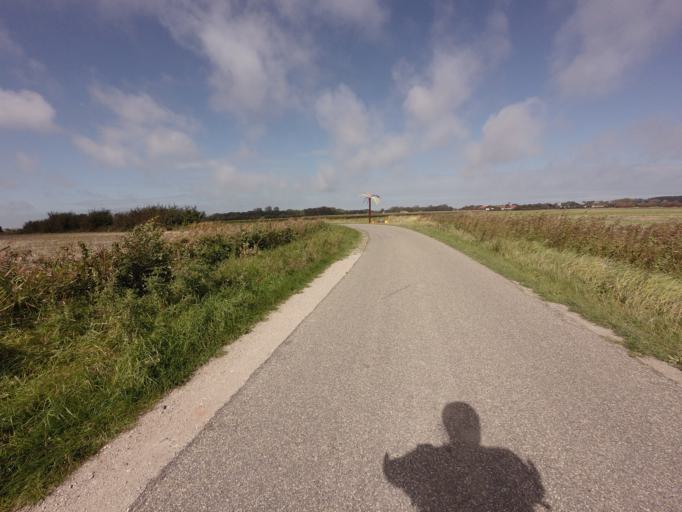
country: NL
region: Zeeland
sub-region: Gemeente Middelburg
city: Middelburg
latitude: 51.5503
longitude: 3.5053
